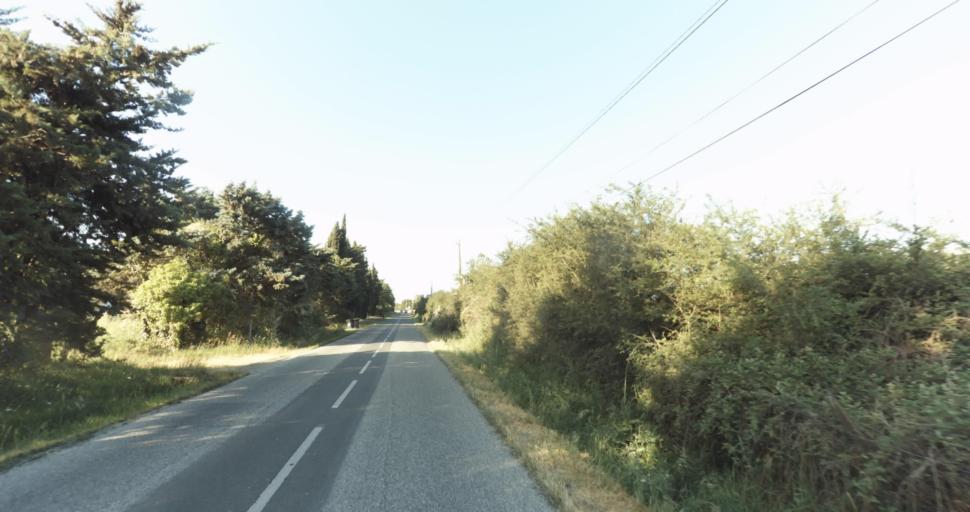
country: FR
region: Midi-Pyrenees
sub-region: Departement de la Haute-Garonne
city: Leguevin
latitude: 43.5716
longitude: 1.2348
